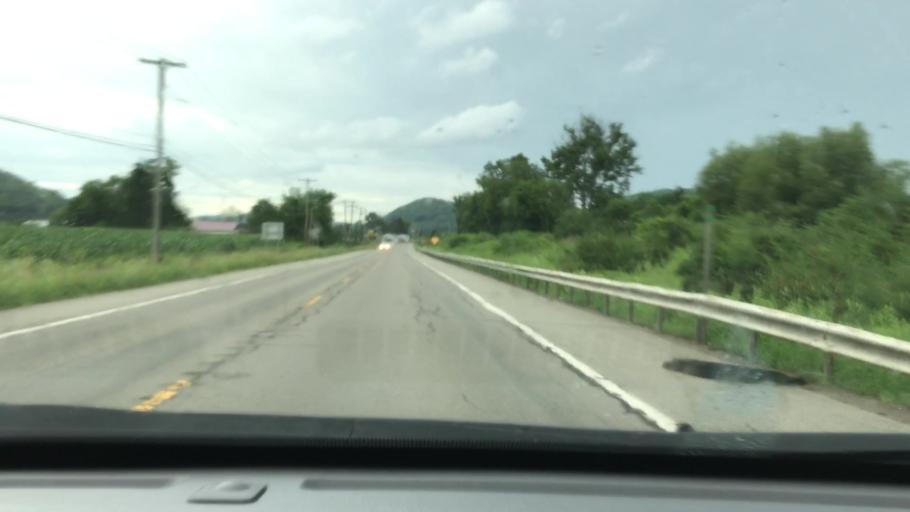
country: US
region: New York
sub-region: Cattaraugus County
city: Salamanca
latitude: 42.2458
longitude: -78.6441
